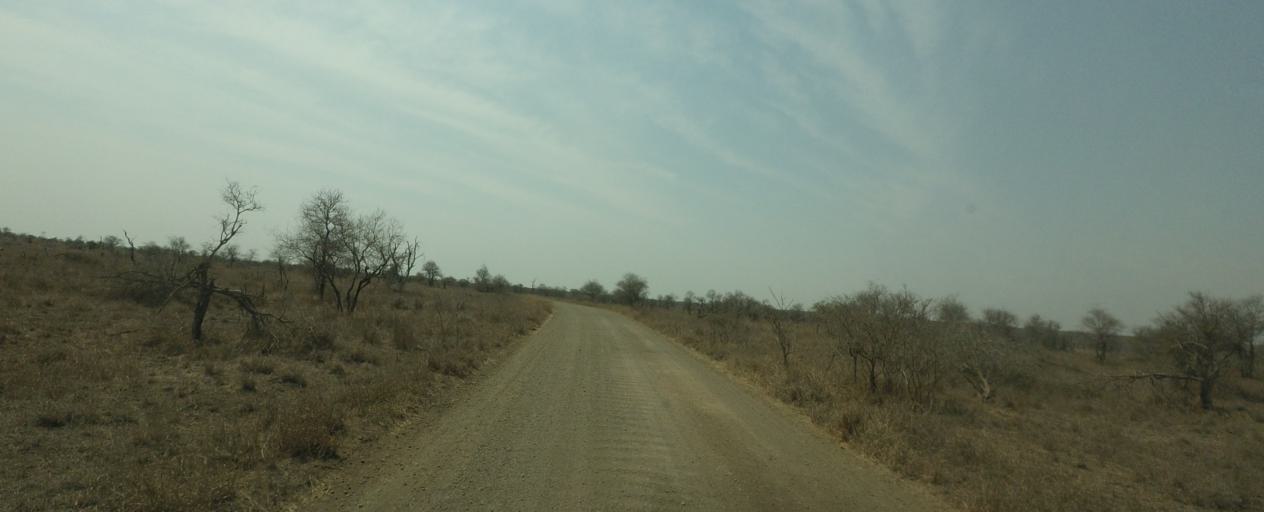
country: ZA
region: Limpopo
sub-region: Mopani District Municipality
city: Phalaborwa
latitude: -24.2603
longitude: 31.6687
